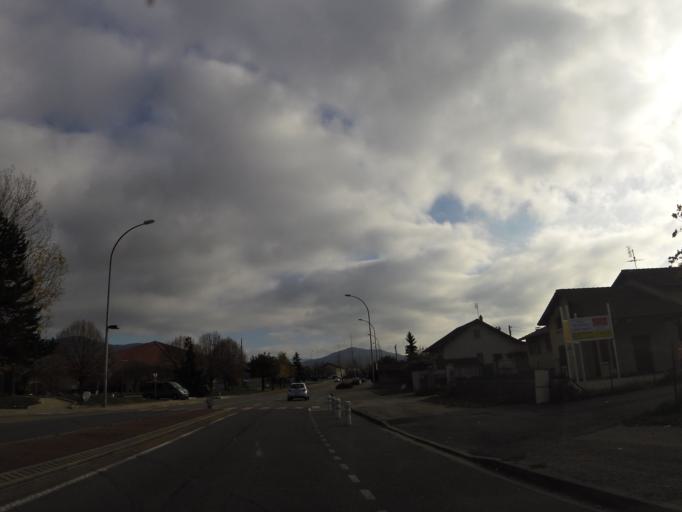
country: FR
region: Rhone-Alpes
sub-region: Departement de l'Ain
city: Amberieu-en-Bugey
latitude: 45.9615
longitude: 5.3468
